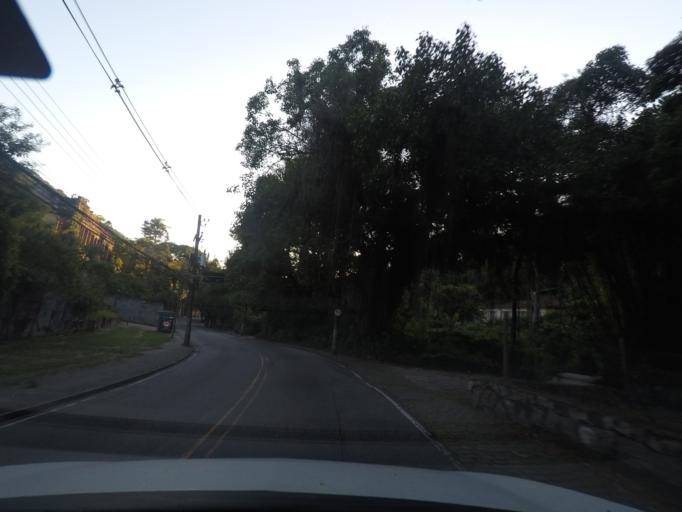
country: BR
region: Rio de Janeiro
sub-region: Rio De Janeiro
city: Rio de Janeiro
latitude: -22.9625
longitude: -43.2749
